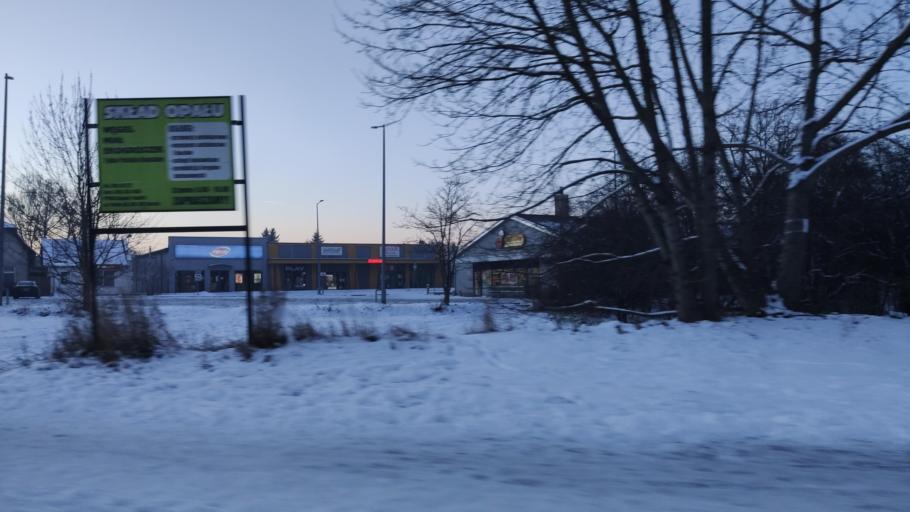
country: PL
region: Kujawsko-Pomorskie
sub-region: Powiat zninski
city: Barcin
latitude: 52.8581
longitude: 17.9421
